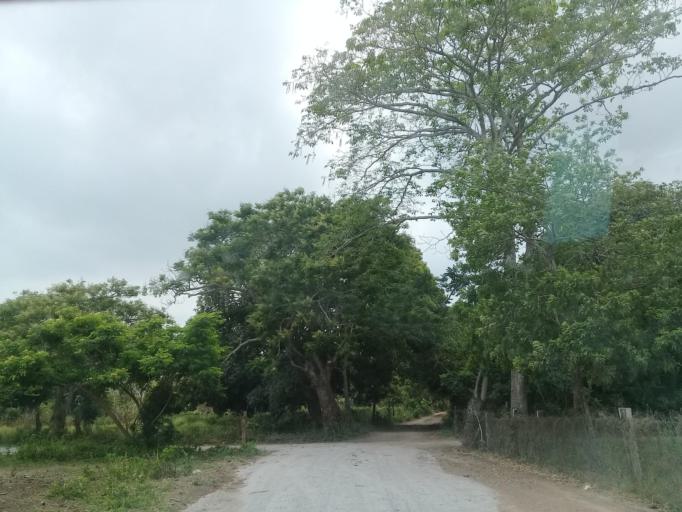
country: MX
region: Veracruz
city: El Tejar
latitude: 19.0434
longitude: -96.1669
